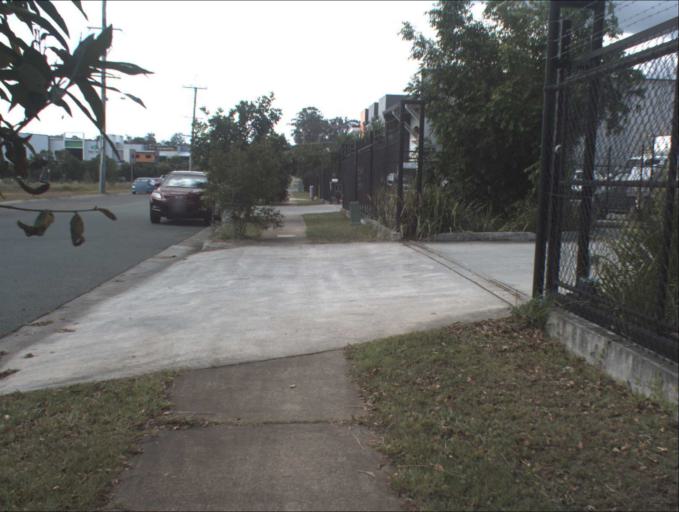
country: AU
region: Queensland
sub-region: Logan
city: Slacks Creek
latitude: -27.6639
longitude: 153.1332
